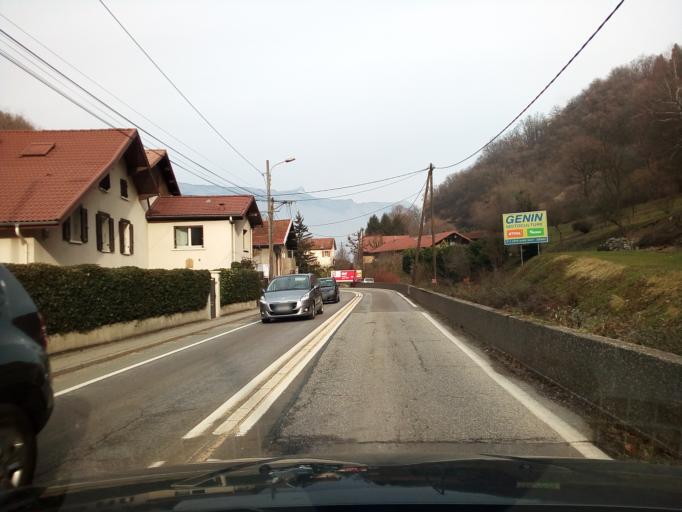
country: FR
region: Rhone-Alpes
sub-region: Departement de l'Isere
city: Gieres
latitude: 45.1744
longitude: 5.7900
